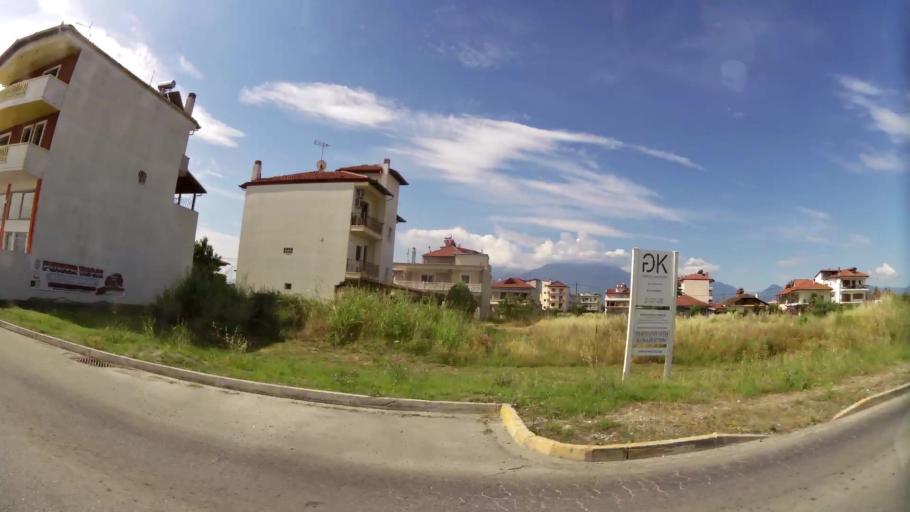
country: GR
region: Central Macedonia
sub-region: Nomos Pierias
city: Katerini
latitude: 40.2807
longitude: 22.4916
